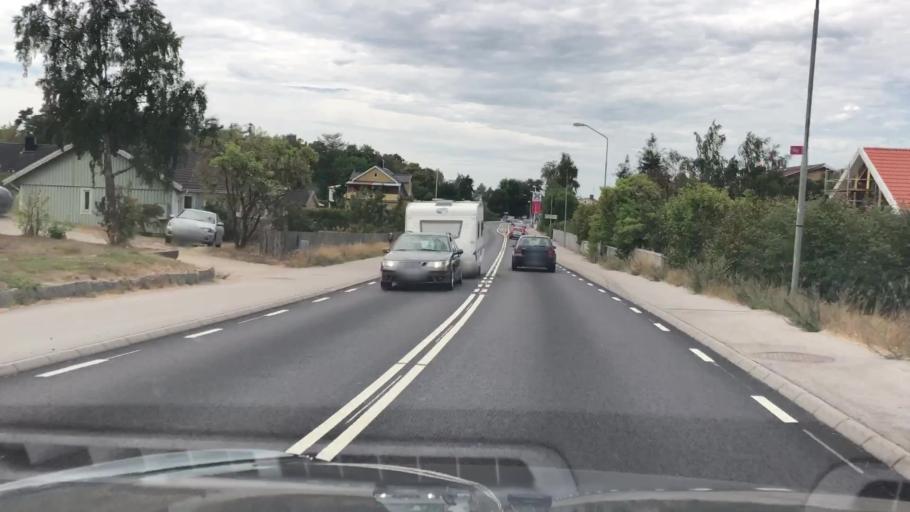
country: SE
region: Blekinge
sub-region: Karlskrona Kommun
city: Jaemjoe
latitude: 56.1931
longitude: 15.8416
